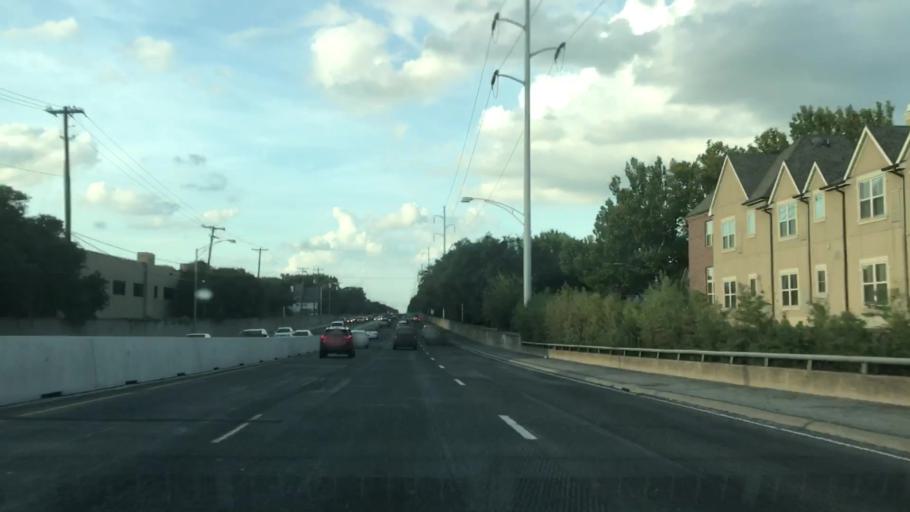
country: US
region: Texas
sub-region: Dallas County
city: Highland Park
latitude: 32.8218
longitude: -96.8167
